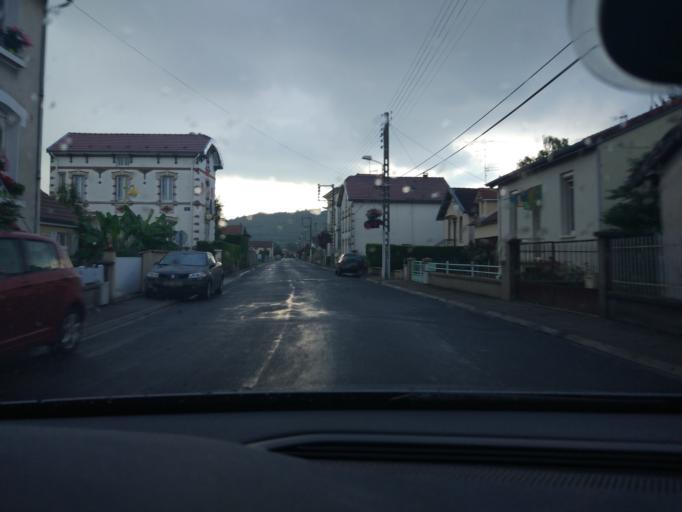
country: FR
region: Lorraine
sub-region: Departement de la Meuse
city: Verdun
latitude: 49.1694
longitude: 5.3936
